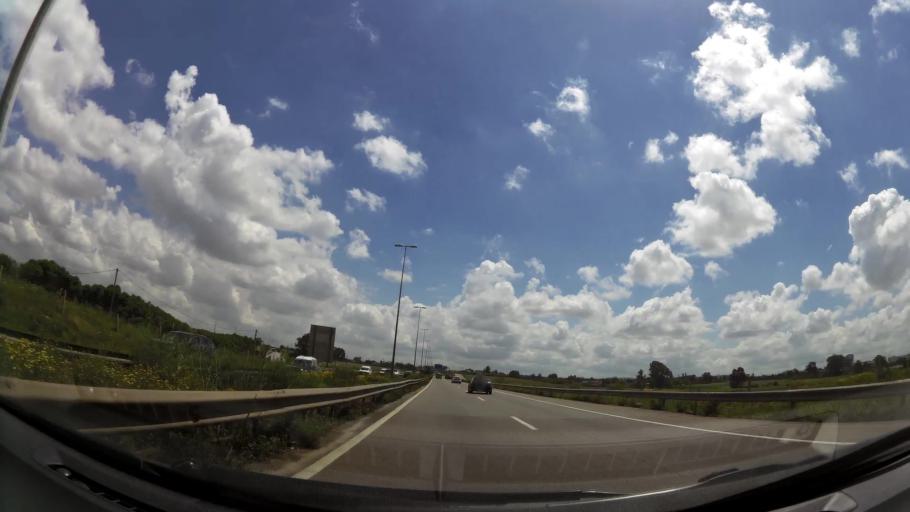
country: MA
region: Grand Casablanca
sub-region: Nouaceur
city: Bouskoura
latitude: 33.4478
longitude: -7.6331
